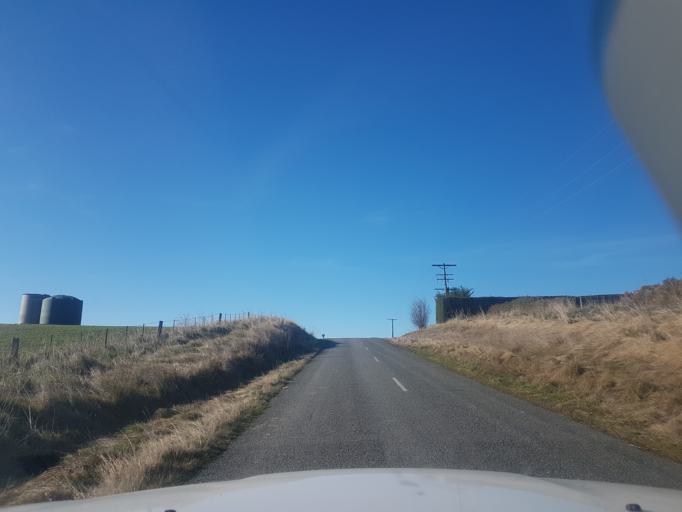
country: NZ
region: Canterbury
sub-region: Timaru District
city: Pleasant Point
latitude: -44.2939
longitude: 171.0509
